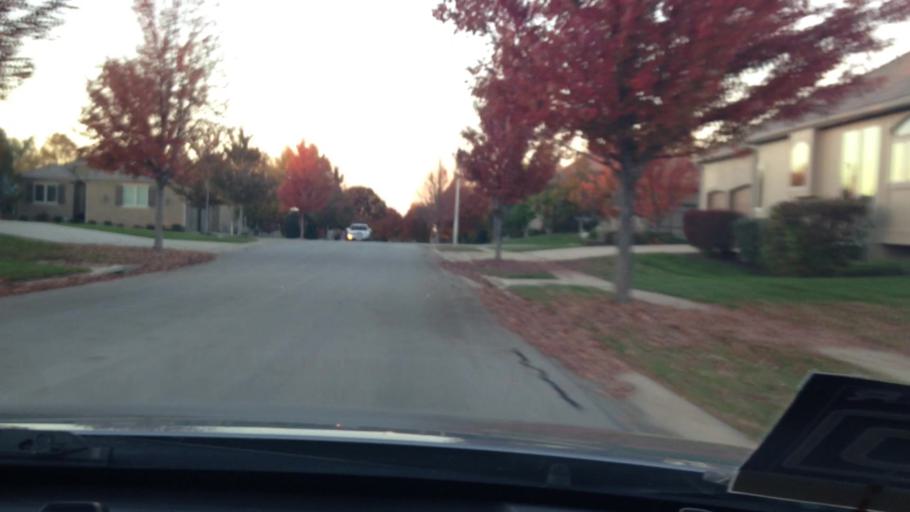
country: US
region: Kansas
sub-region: Johnson County
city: Lenexa
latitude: 38.8655
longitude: -94.7208
